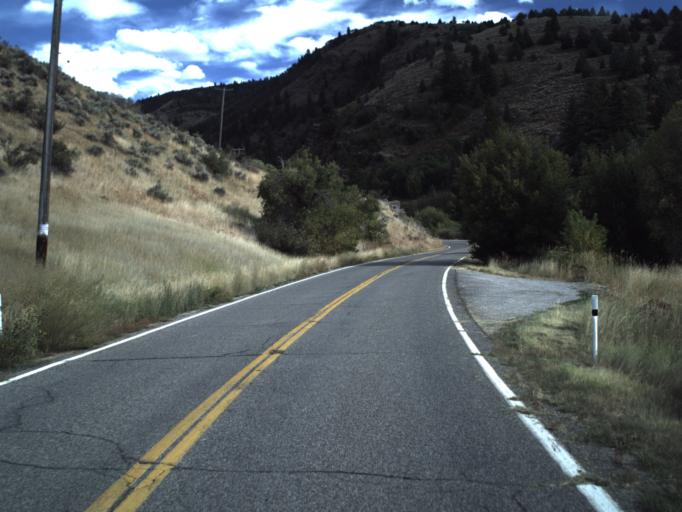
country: US
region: Utah
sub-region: Cache County
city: Millville
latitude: 41.6132
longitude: -111.6339
